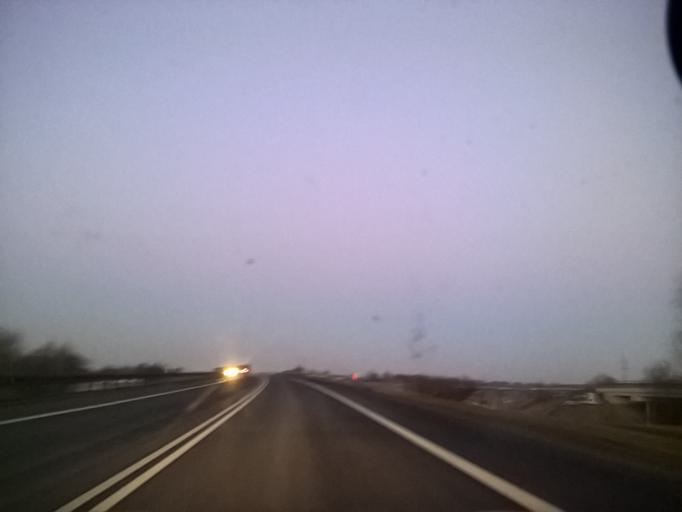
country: PL
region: Warmian-Masurian Voivodeship
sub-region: Powiat olsztynski
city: Biskupiec
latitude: 53.8344
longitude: 20.9230
